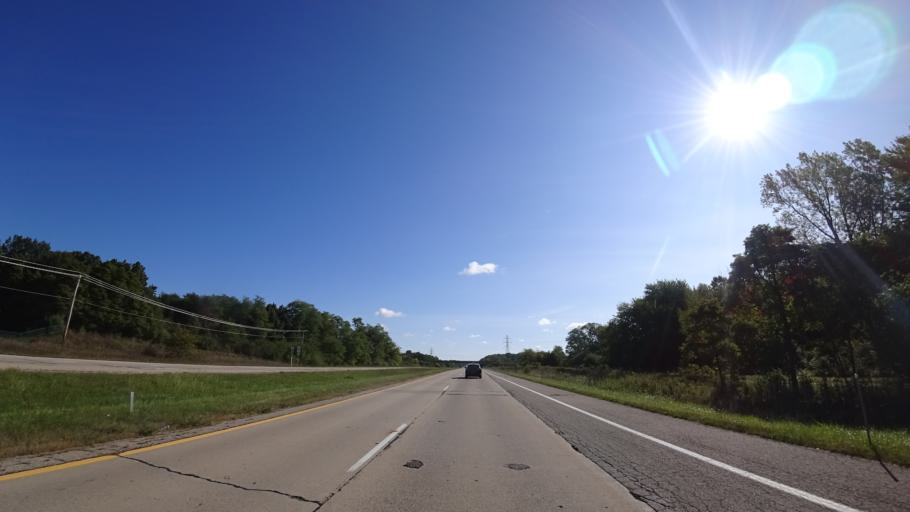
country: US
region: Michigan
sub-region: Berrien County
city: Benton Heights
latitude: 42.1191
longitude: -86.4121
